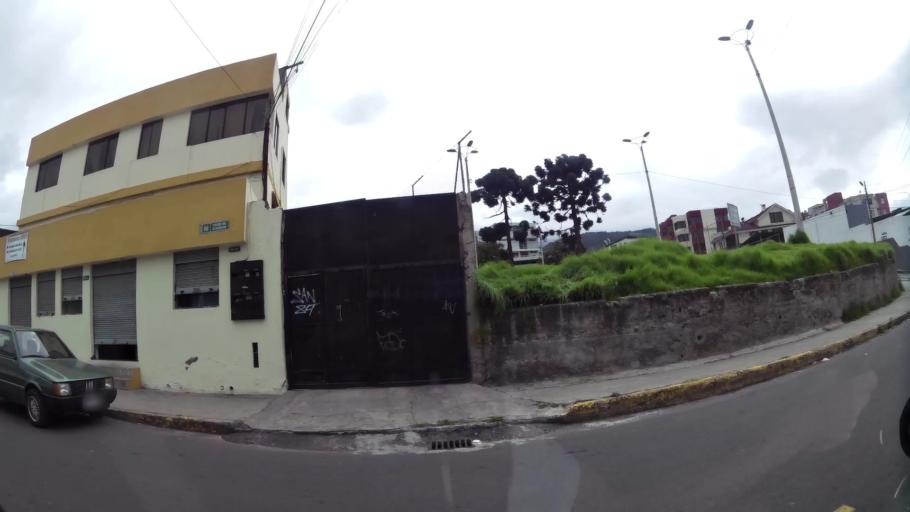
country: EC
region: Pichincha
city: Quito
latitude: -0.1226
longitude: -78.5023
